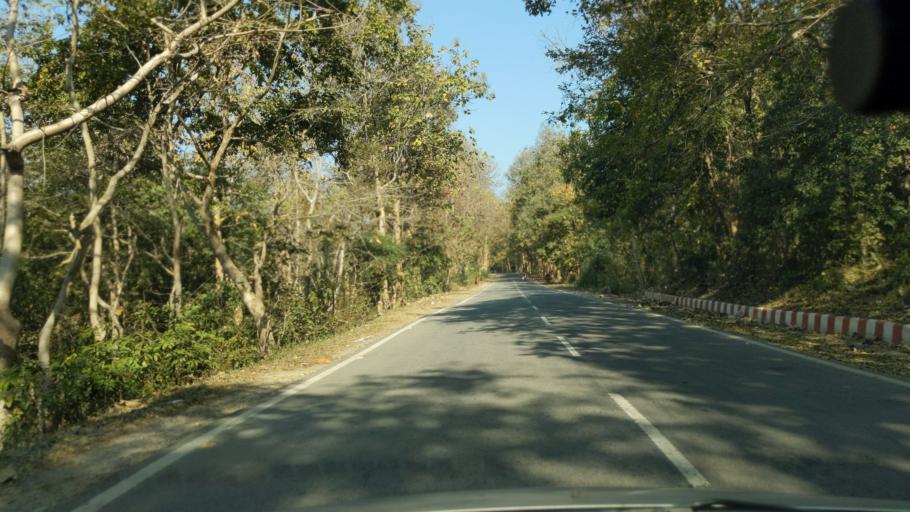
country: IN
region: Uttarakhand
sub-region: Naini Tal
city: Ramnagar
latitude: 29.3951
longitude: 79.1372
